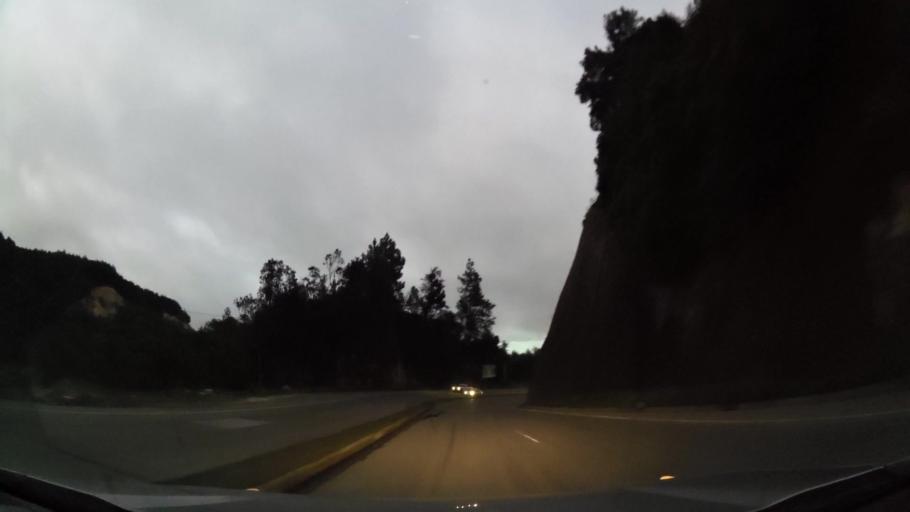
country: GT
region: Chimaltenango
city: Santa Apolonia
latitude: 14.8190
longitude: -91.0028
